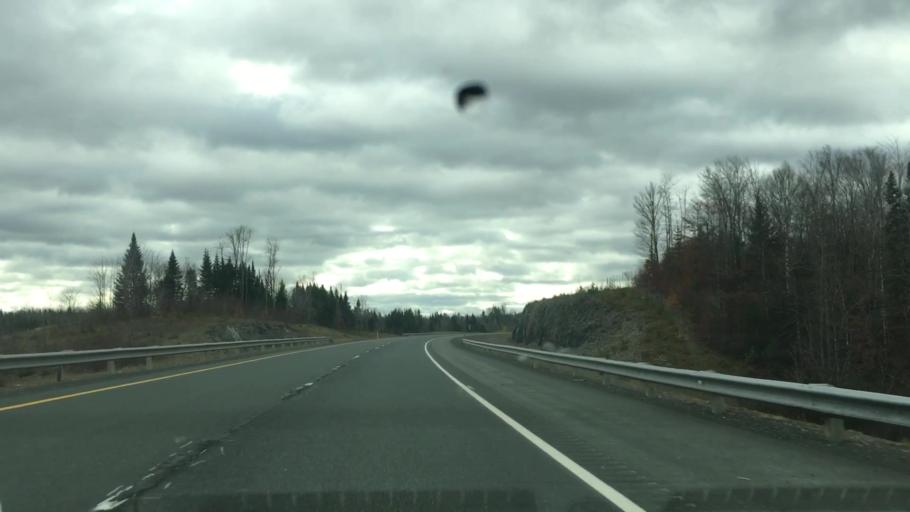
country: US
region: Maine
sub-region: Aroostook County
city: Easton
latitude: 46.6218
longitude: -67.7387
